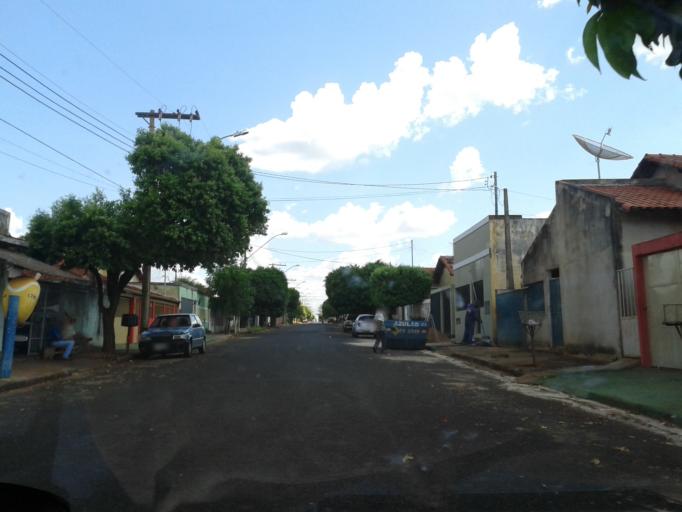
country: BR
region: Minas Gerais
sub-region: Ituiutaba
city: Ituiutaba
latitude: -18.9837
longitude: -49.4496
